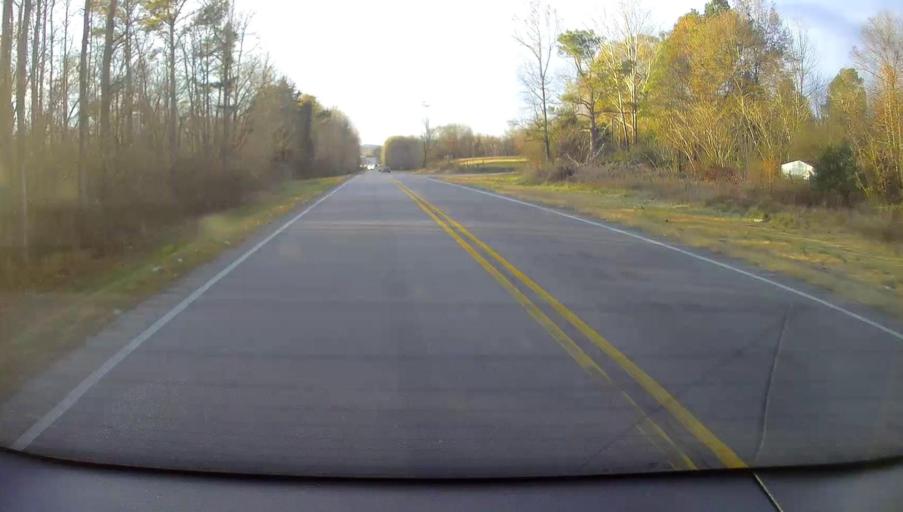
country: US
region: Alabama
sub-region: Blount County
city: Blountsville
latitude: 34.1552
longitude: -86.4595
